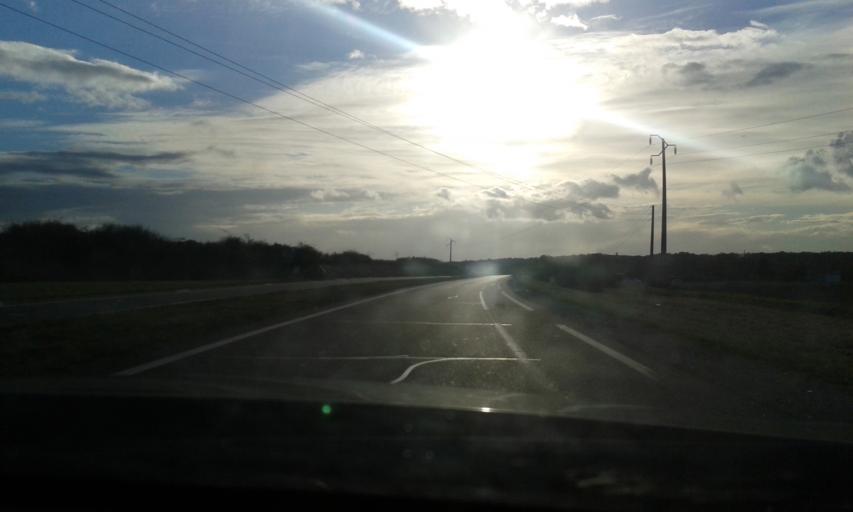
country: FR
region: Centre
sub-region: Departement d'Eure-et-Loir
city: Leves
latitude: 48.4874
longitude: 1.4701
